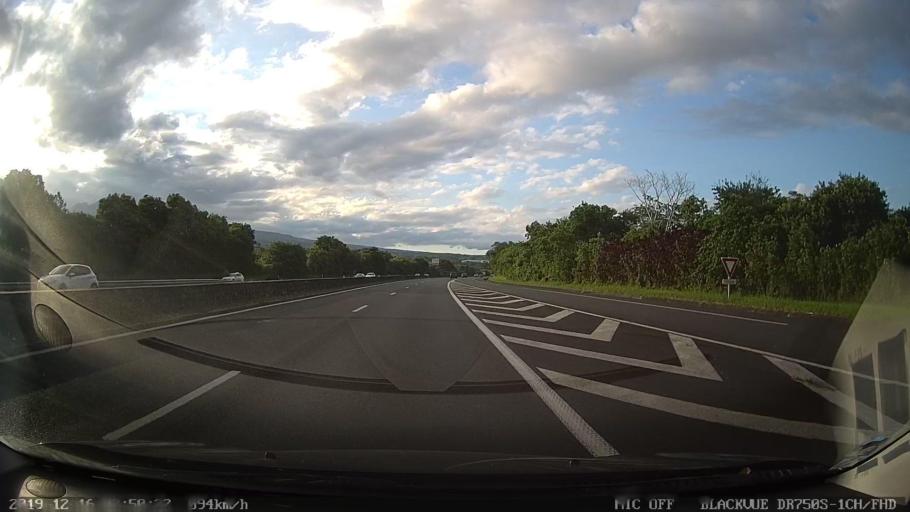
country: RE
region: Reunion
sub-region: Reunion
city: Bras-Panon
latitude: -21.0133
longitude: 55.6918
